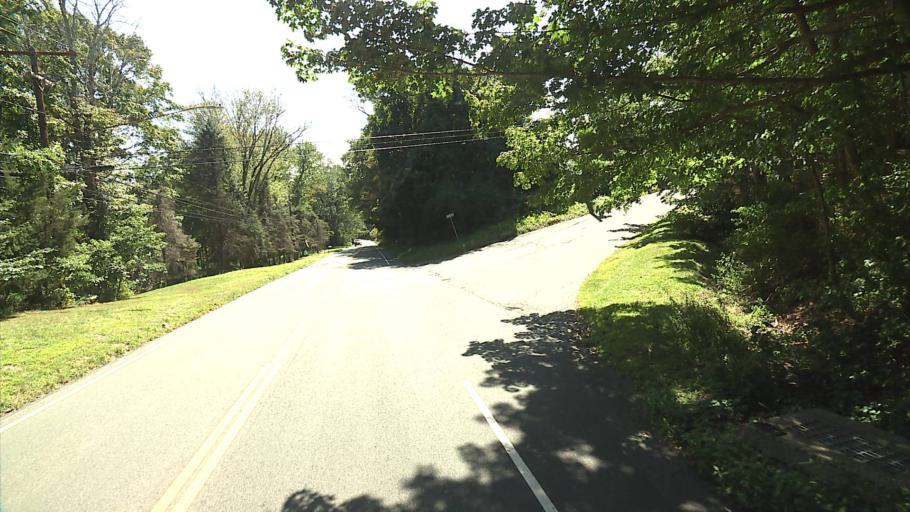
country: US
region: Connecticut
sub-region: New Haven County
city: Oxford
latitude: 41.4009
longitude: -73.1410
